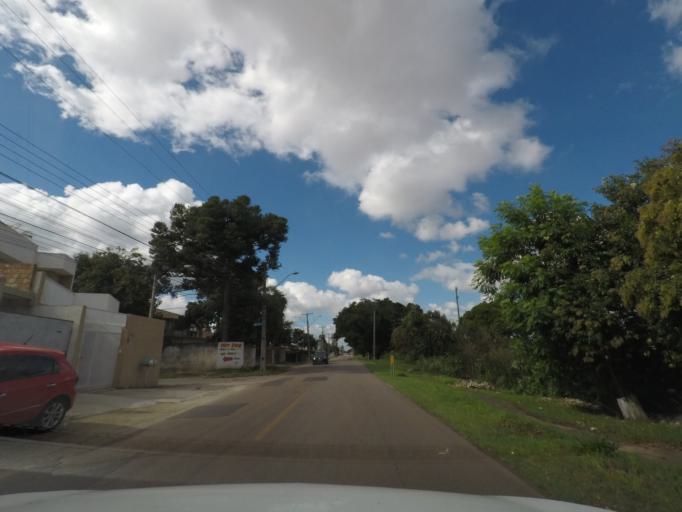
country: BR
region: Parana
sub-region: Curitiba
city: Curitiba
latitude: -25.4747
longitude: -49.2432
